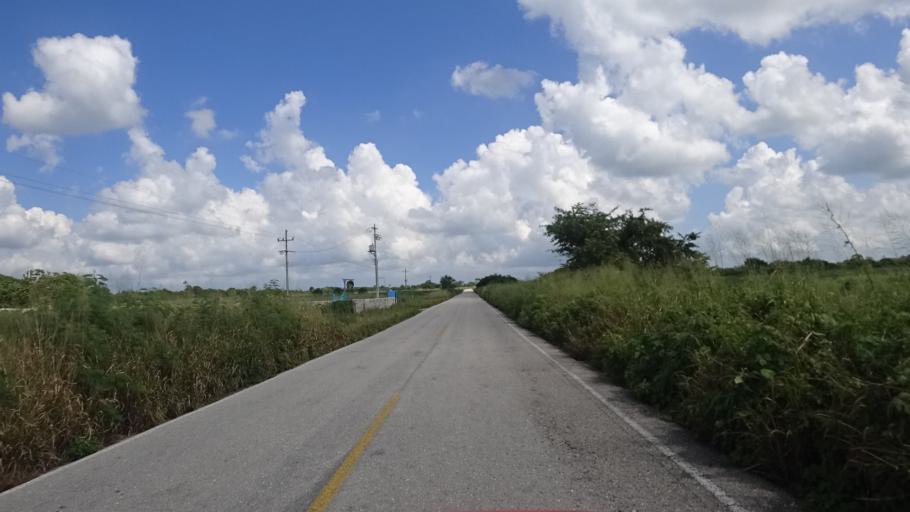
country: MX
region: Yucatan
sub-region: Panaba
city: Loche
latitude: 21.4369
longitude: -88.1406
